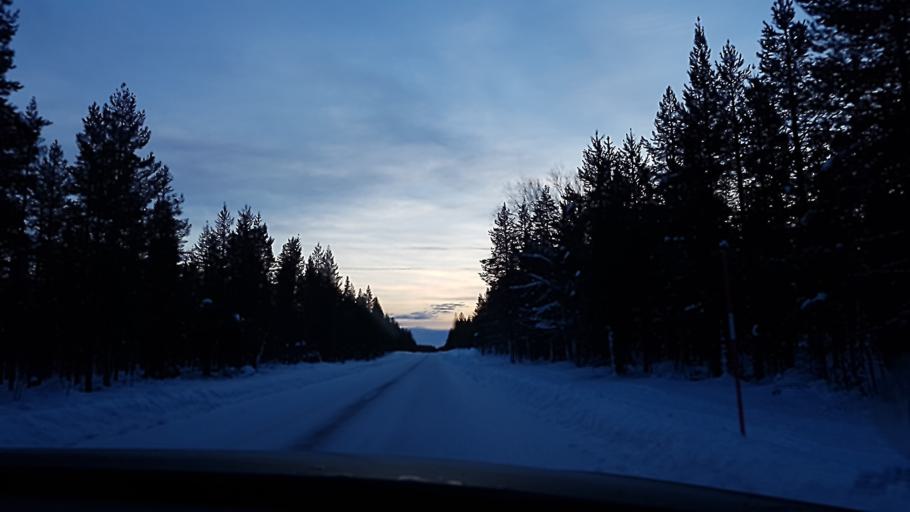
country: SE
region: Norrbotten
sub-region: Arvidsjaurs Kommun
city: Arvidsjaur
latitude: 65.9171
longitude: 19.4594
